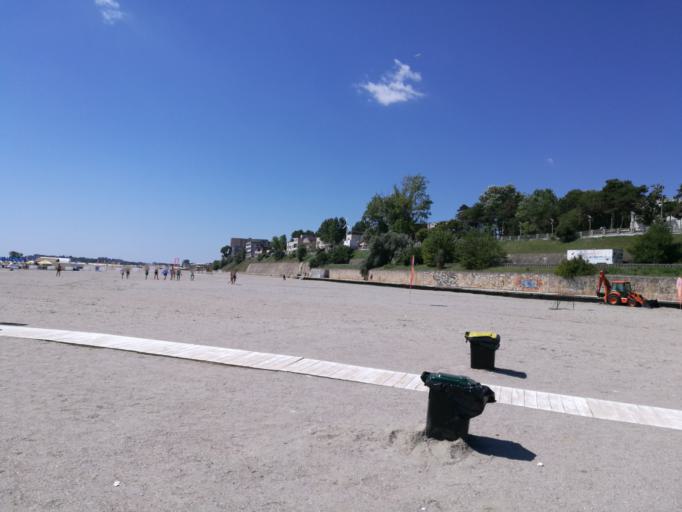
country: RO
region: Constanta
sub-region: Oras Eforie
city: Eforie Nord
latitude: 44.0686
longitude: 28.6398
